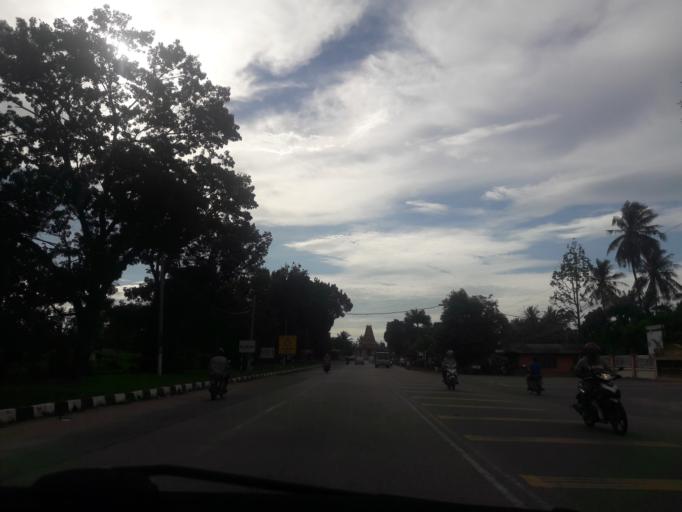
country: MY
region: Kedah
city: Sungai Petani
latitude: 5.6308
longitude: 100.5211
